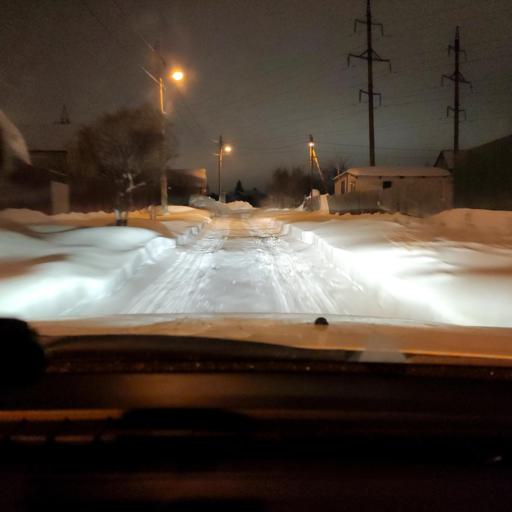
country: RU
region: Samara
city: Petra-Dubrava
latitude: 53.2901
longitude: 50.3133
